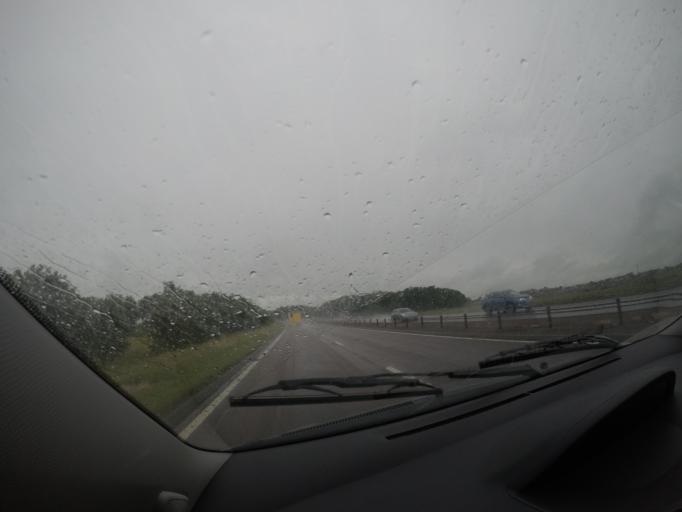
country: GB
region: Scotland
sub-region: Dundee City
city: Dundee
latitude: 56.5371
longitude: -2.9463
